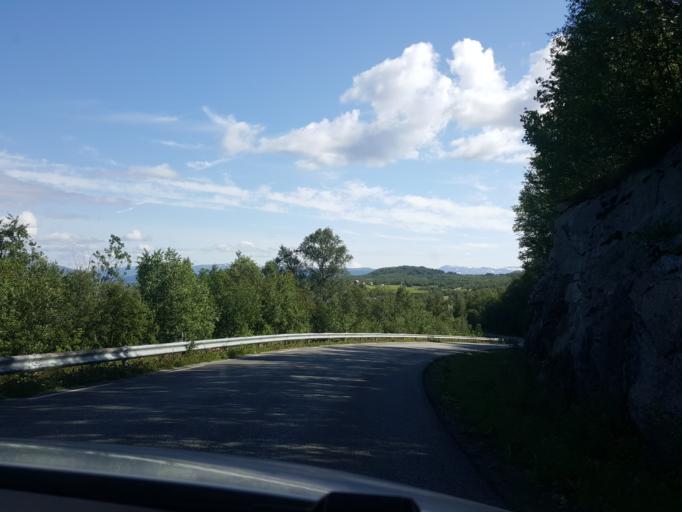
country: NO
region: Nordland
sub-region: Bodo
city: Loding
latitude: 67.2277
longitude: 14.8821
